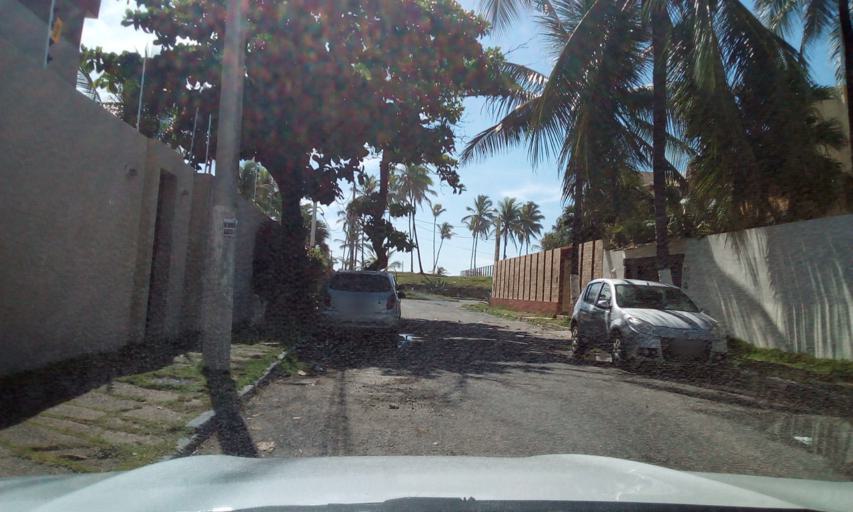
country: BR
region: Bahia
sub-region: Lauro De Freitas
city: Lauro de Freitas
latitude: -12.8876
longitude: -38.2878
